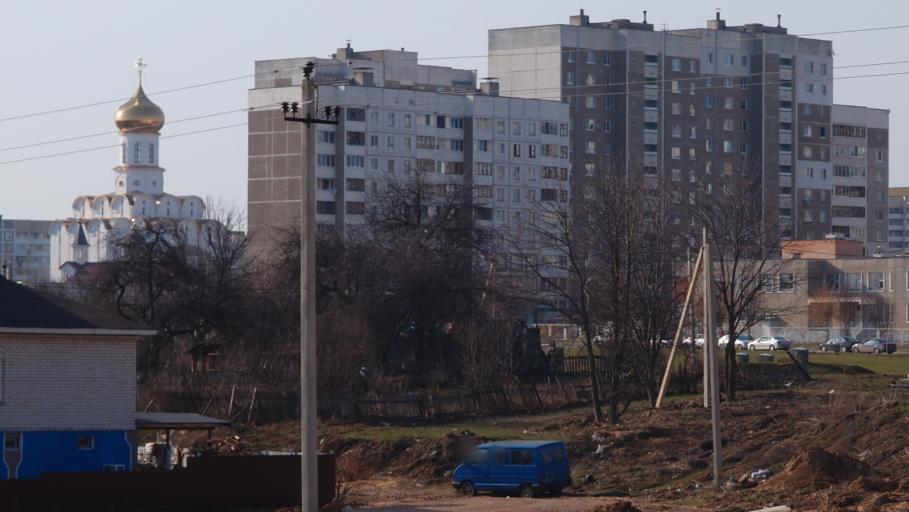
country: BY
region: Minsk
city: Novoye Medvezhino
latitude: 53.8769
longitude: 27.4486
